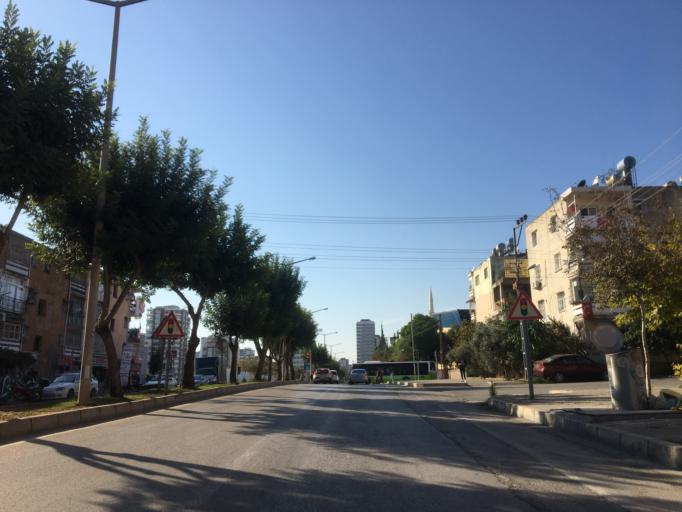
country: TR
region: Adana
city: Seyhan
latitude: 37.0291
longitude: 35.2665
